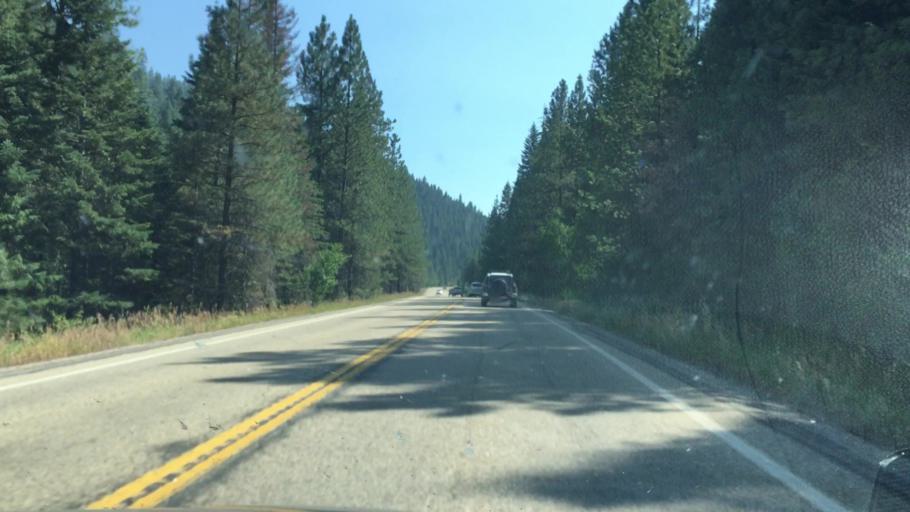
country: US
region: Idaho
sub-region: Valley County
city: Cascade
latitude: 44.2350
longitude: -116.1039
